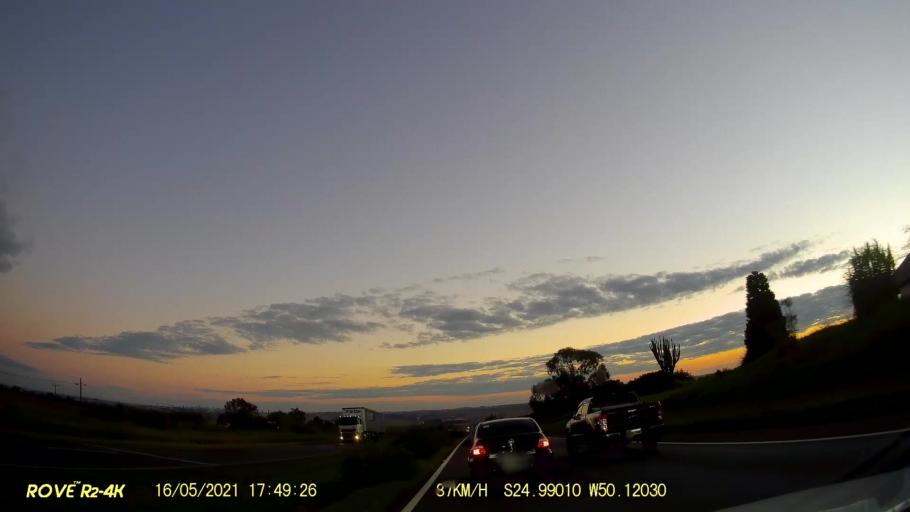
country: BR
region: Parana
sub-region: Carambei
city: Carambei
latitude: -24.9903
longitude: -50.1206
